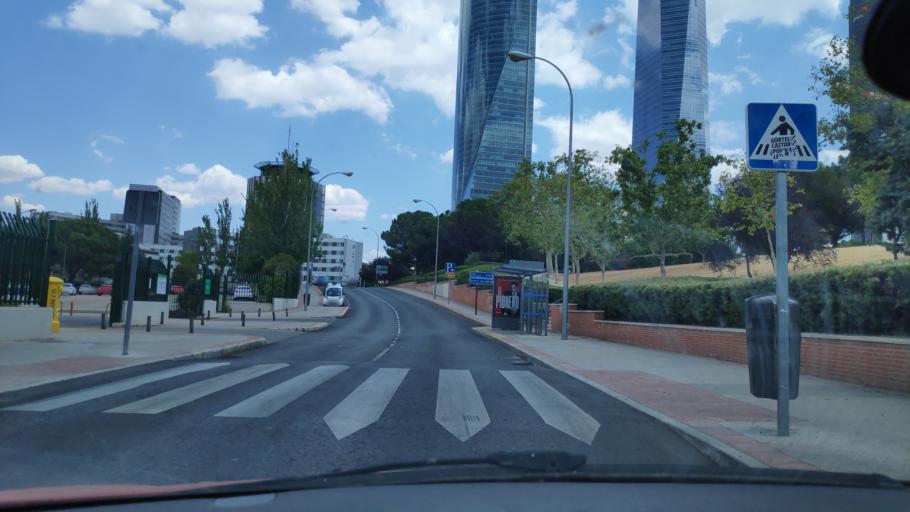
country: ES
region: Madrid
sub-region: Provincia de Madrid
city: Pinar de Chamartin
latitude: 40.4809
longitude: -3.6913
